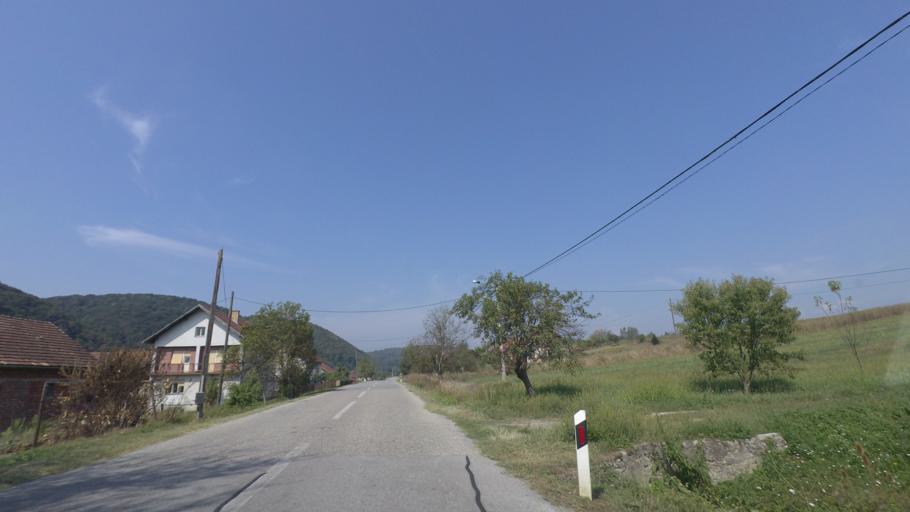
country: HR
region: Sisacko-Moslavacka
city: Dvor
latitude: 45.0891
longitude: 16.3061
